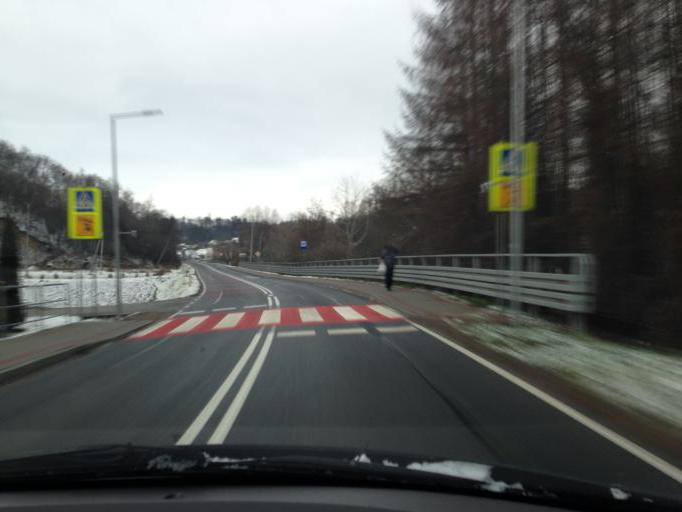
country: PL
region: Lesser Poland Voivodeship
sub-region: Powiat tarnowski
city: Rzepiennik Strzyzewski
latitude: 49.8064
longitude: 21.0355
